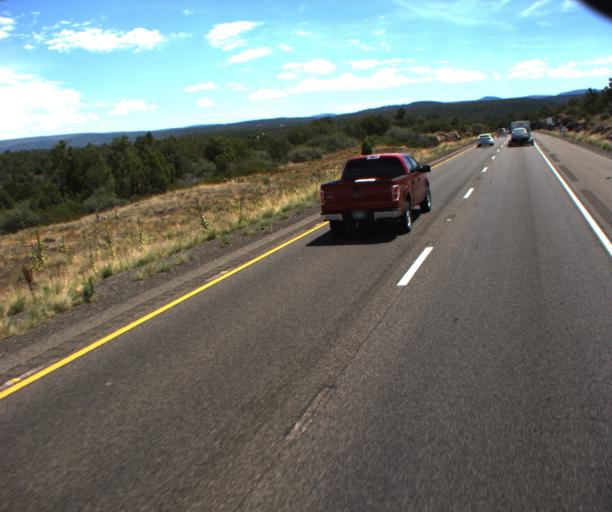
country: US
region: Arizona
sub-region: Yavapai County
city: Village of Oak Creek (Big Park)
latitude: 34.7678
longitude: -111.6467
